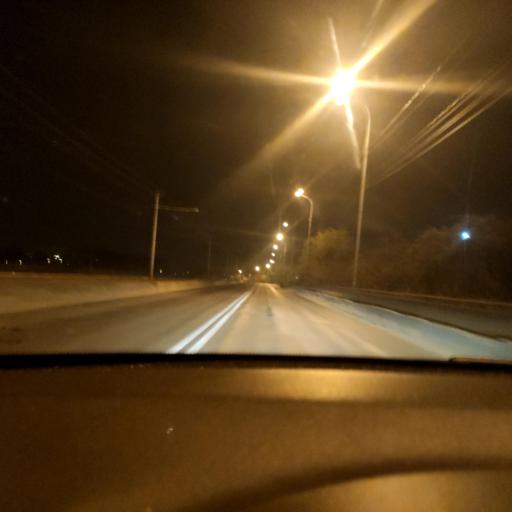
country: RU
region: Samara
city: Smyshlyayevka
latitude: 53.2196
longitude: 50.2902
